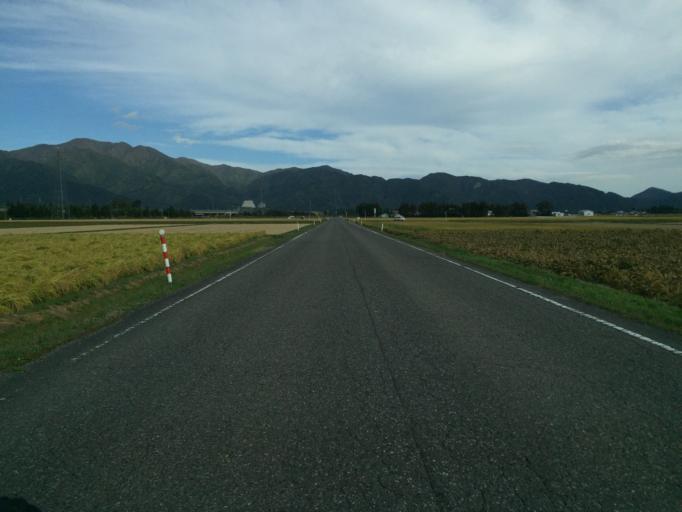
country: JP
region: Fukushima
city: Inawashiro
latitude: 37.5432
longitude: 140.0969
